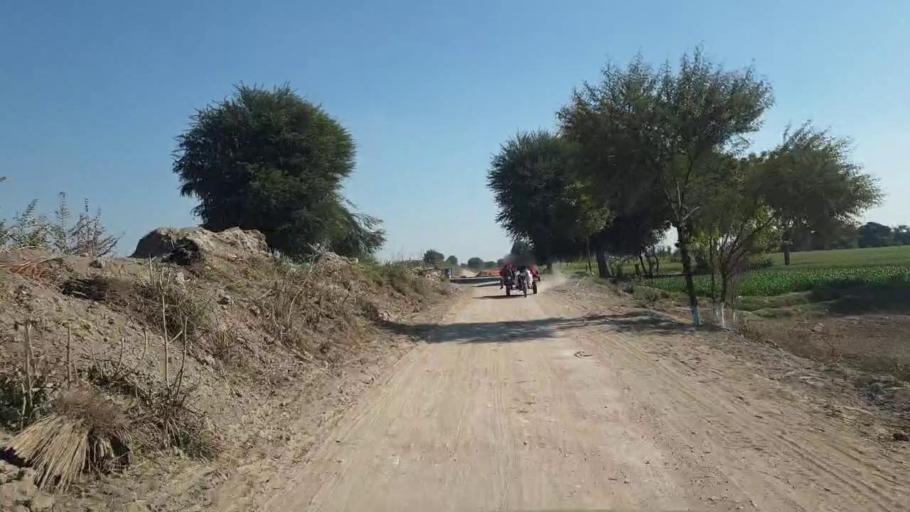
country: PK
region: Sindh
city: Shahpur Chakar
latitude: 26.1470
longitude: 68.6447
